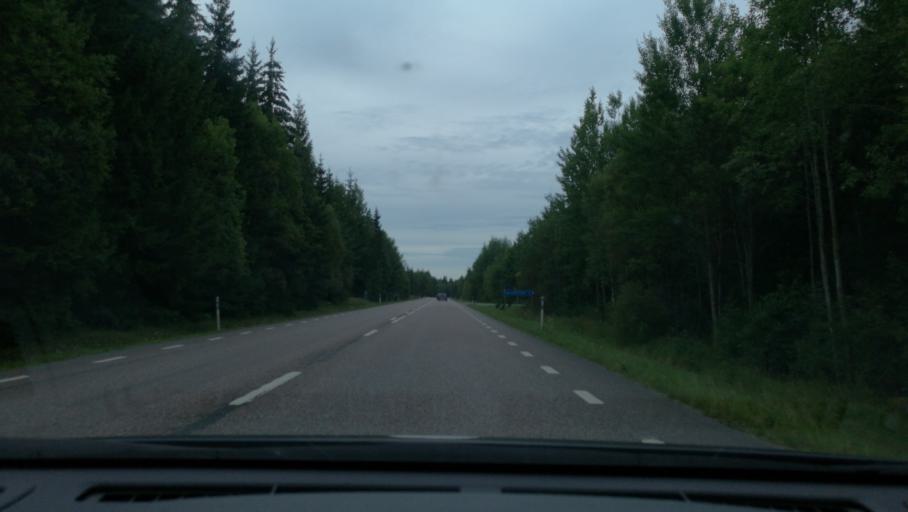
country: SE
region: Soedermanland
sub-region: Katrineholms Kommun
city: Katrineholm
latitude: 59.0275
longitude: 16.2138
